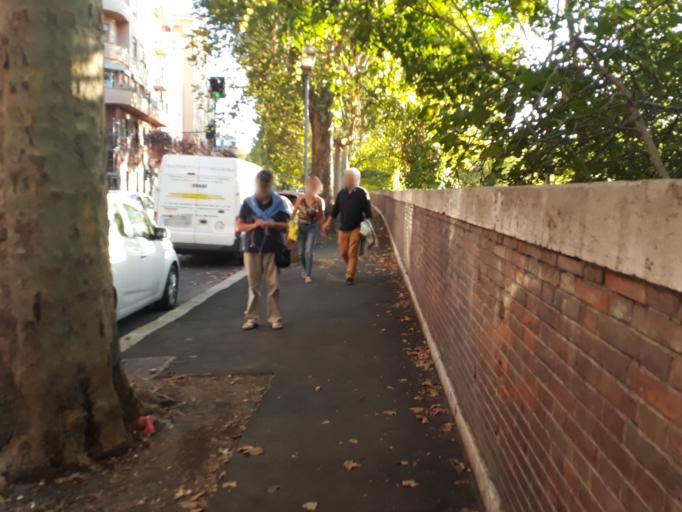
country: VA
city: Vatican City
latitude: 41.8812
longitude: 12.4733
